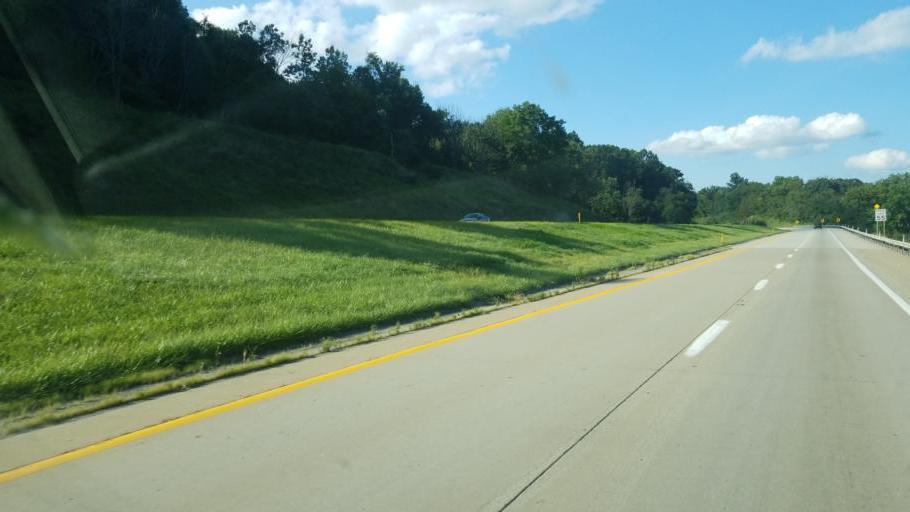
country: US
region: Pennsylvania
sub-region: Greene County
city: Waynesburg
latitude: 39.9460
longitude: -80.1666
